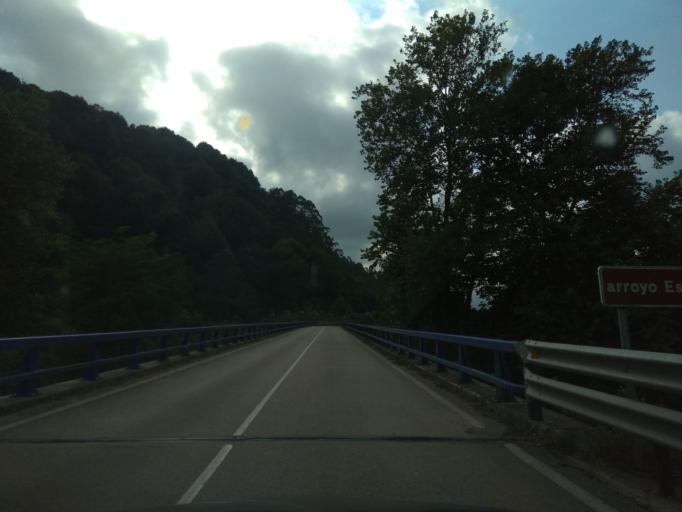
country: ES
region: Cantabria
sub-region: Provincia de Cantabria
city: Comillas
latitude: 43.3221
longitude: -4.3221
